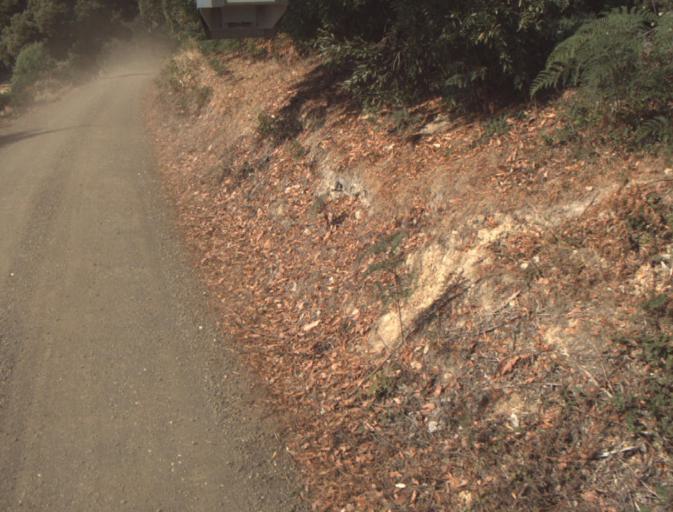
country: AU
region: Tasmania
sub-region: Launceston
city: Mayfield
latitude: -41.1624
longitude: 147.2115
